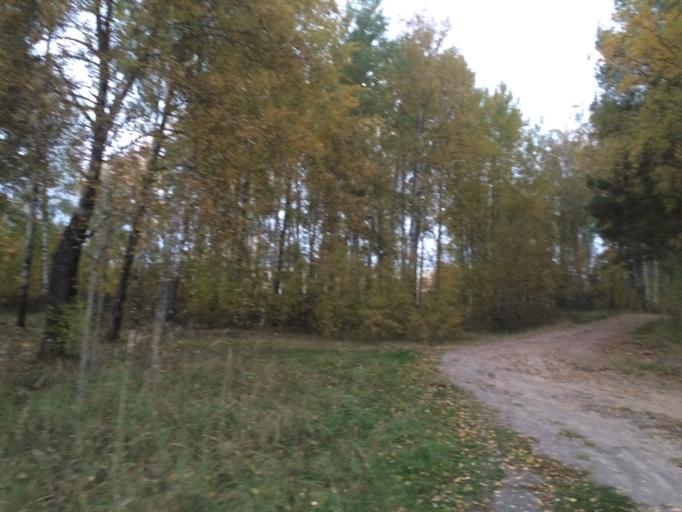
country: RU
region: Nizjnij Novgorod
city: Sarov
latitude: 54.9417
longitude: 43.3413
